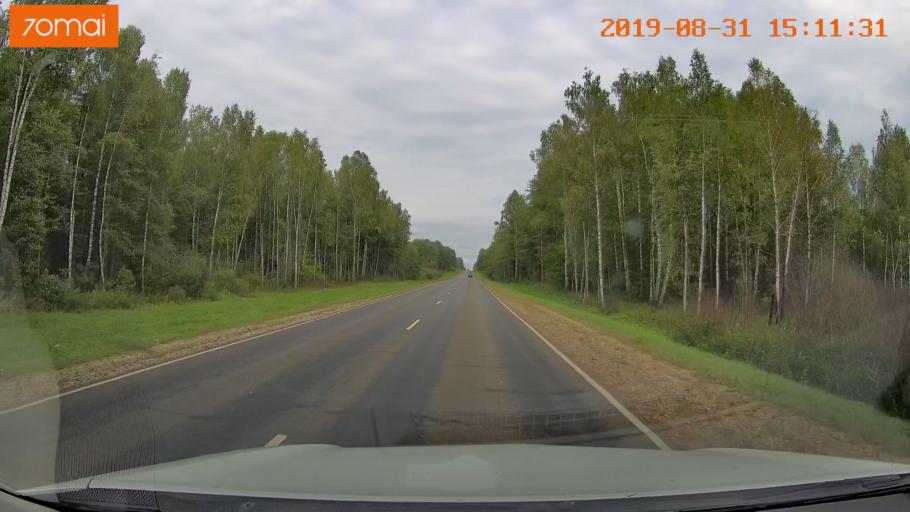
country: RU
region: Kaluga
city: Spas-Demensk
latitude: 54.4230
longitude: 34.2452
